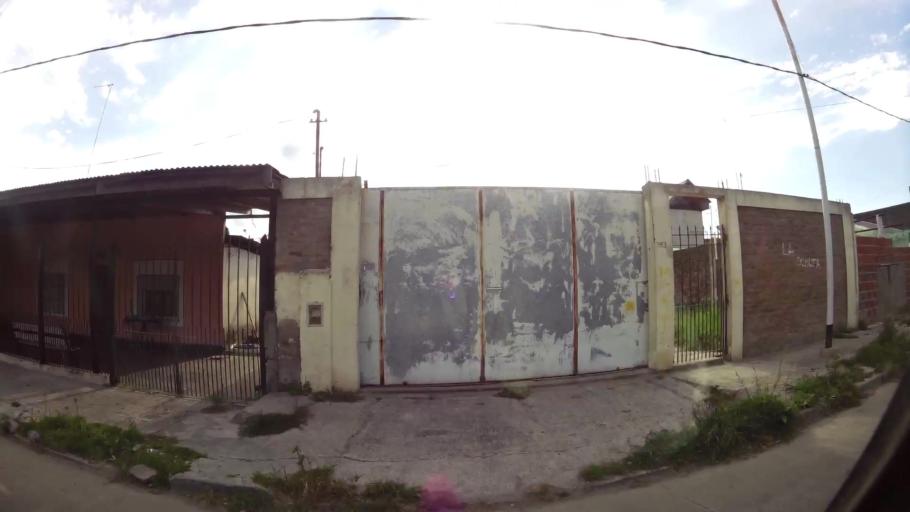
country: AR
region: Buenos Aires
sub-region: Partido de Lanus
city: Lanus
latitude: -34.7046
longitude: -58.3583
